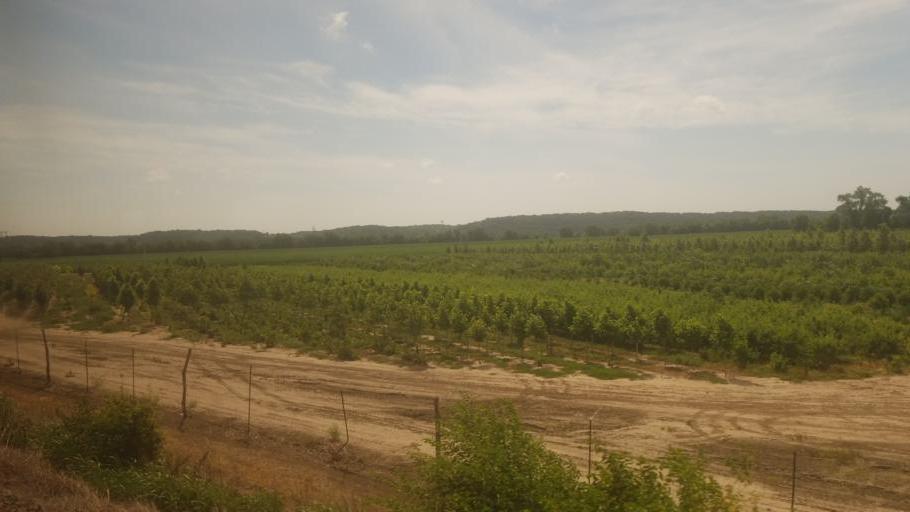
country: US
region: Missouri
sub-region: Jackson County
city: East Independence
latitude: 39.1768
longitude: -94.3272
